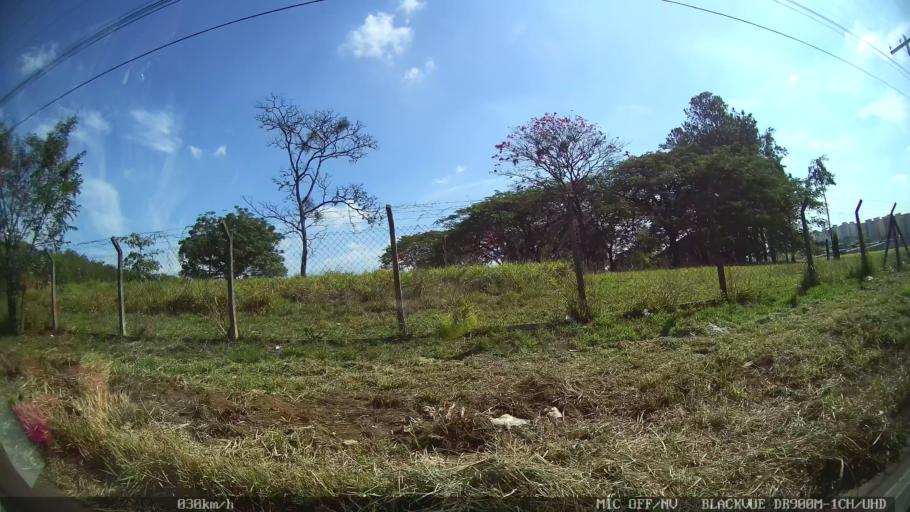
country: BR
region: Sao Paulo
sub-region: Hortolandia
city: Hortolandia
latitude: -22.8376
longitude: -47.2067
